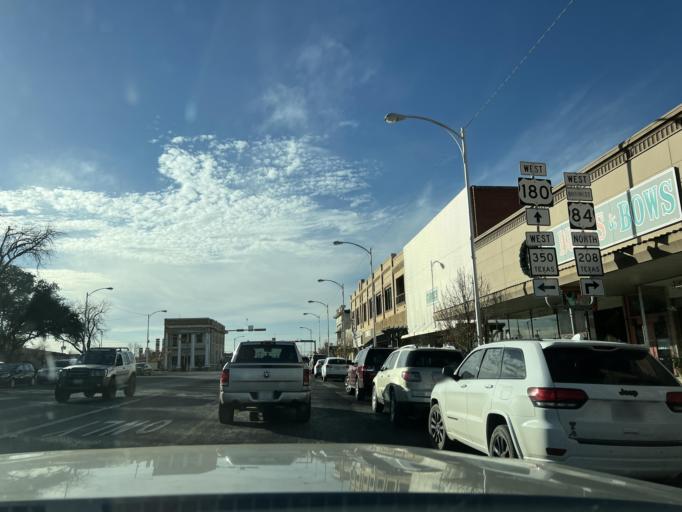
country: US
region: Texas
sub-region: Scurry County
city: Snyder
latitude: 32.7172
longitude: -100.9173
